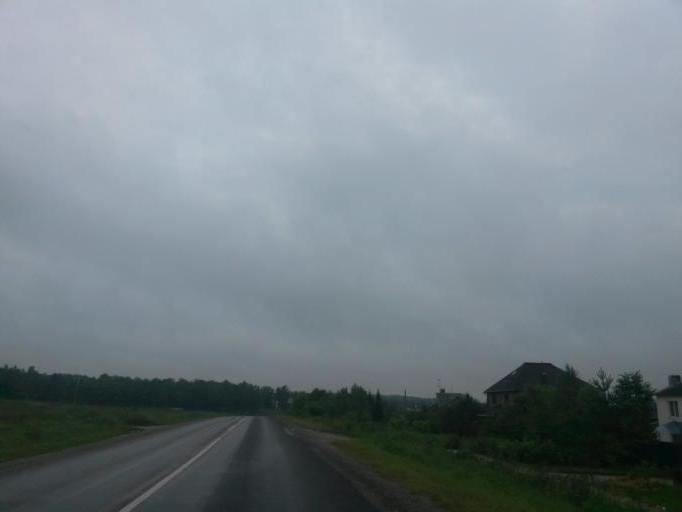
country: RU
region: Moskovskaya
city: Lyubuchany
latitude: 55.3008
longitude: 37.6371
